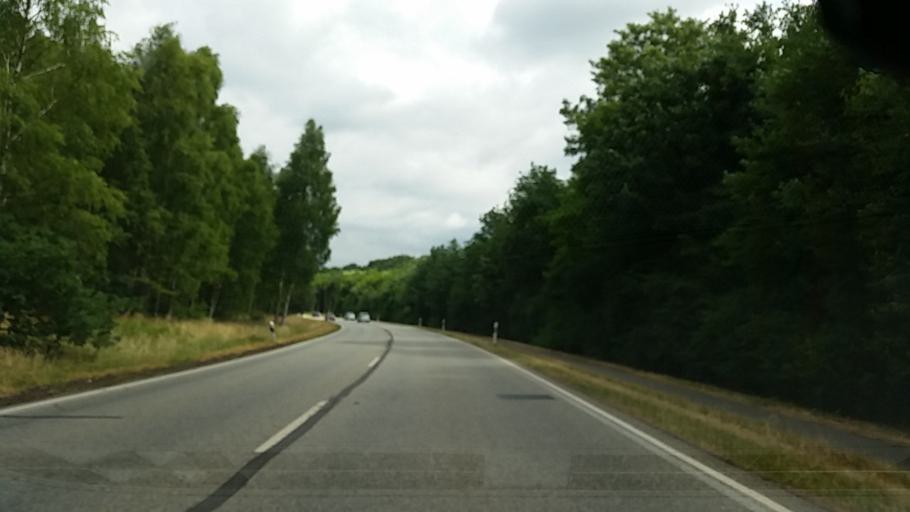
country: DE
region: Schleswig-Holstein
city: Kayhude
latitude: 53.7405
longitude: 10.1201
